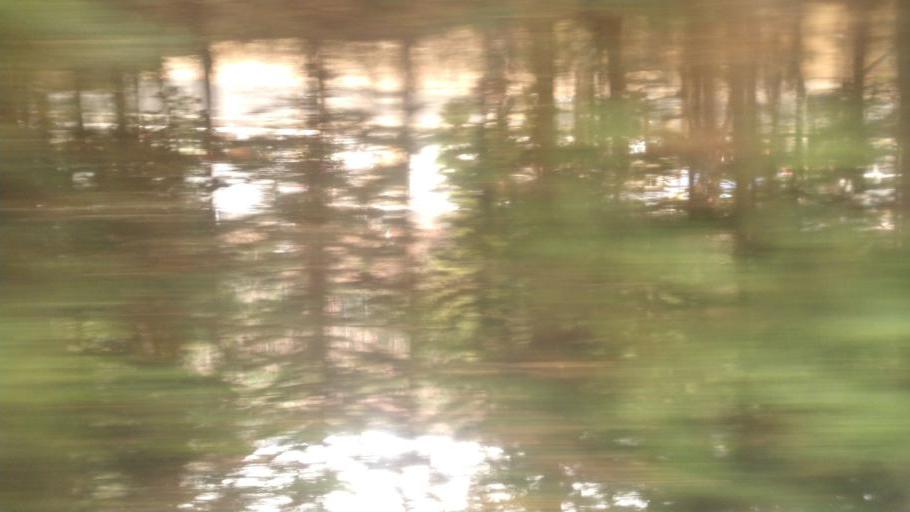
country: JP
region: Nagano
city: Tatsuno
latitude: 35.9749
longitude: 137.8238
